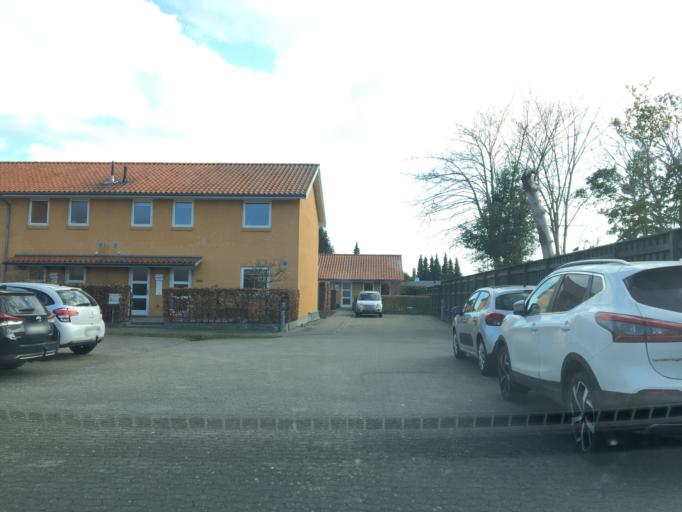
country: DK
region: Capital Region
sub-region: Dragor Kommune
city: Dragor
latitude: 55.5936
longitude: 12.6654
